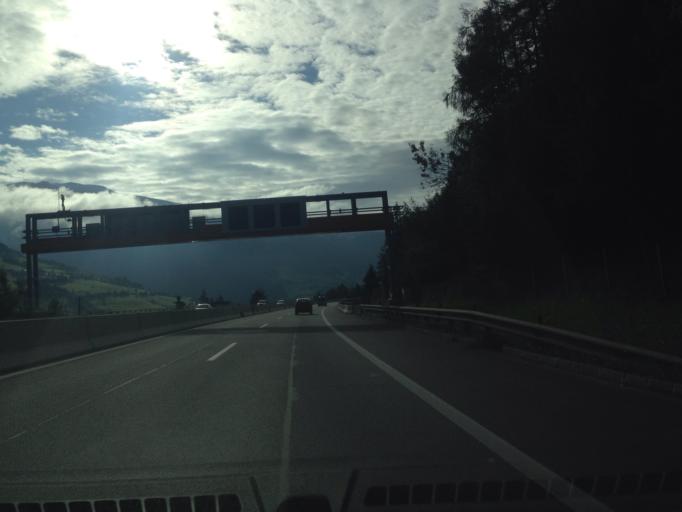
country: AT
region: Tyrol
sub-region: Politischer Bezirk Innsbruck Land
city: Schoenberg im Stubaital
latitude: 47.1738
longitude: 11.4218
